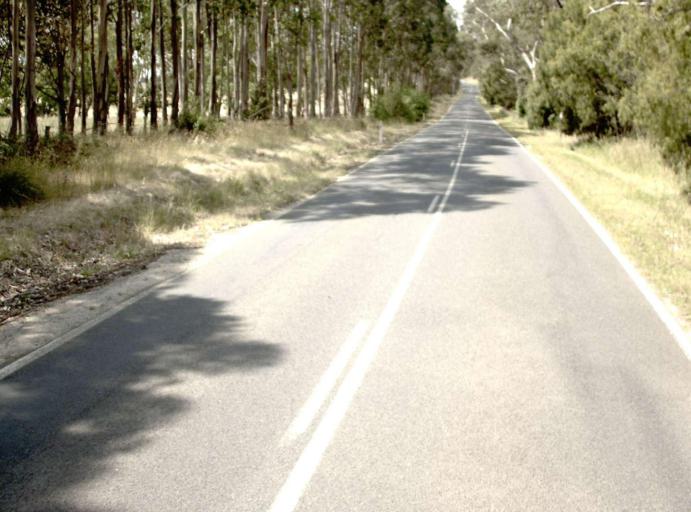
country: AU
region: Victoria
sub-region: Latrobe
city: Traralgon
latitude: -38.2822
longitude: 146.5465
